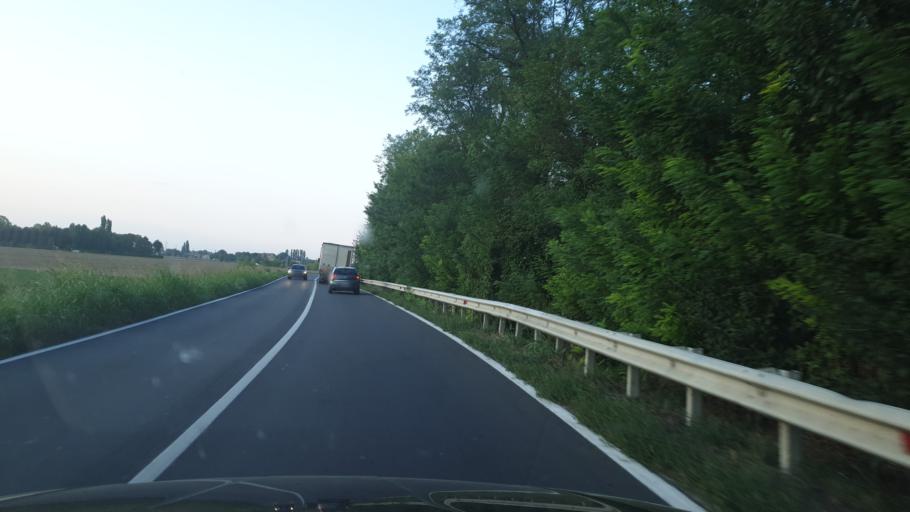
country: IT
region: Emilia-Romagna
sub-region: Provincia di Bologna
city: Progresso
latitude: 44.5540
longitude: 11.3899
